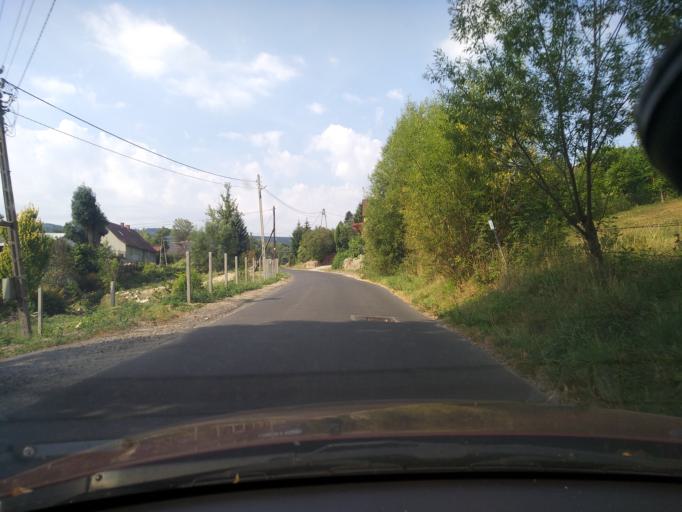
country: PL
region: Lower Silesian Voivodeship
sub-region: Powiat jeleniogorski
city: Stara Kamienica
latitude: 50.8934
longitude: 15.5554
